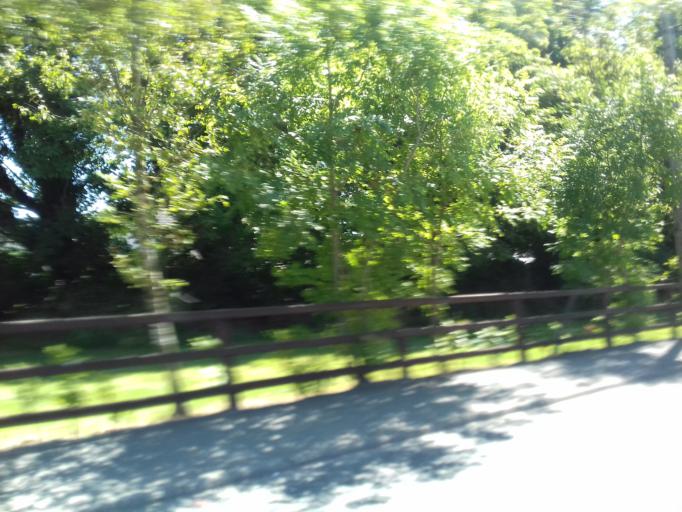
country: IE
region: Leinster
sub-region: Fingal County
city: Swords
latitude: 53.5170
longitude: -6.2668
